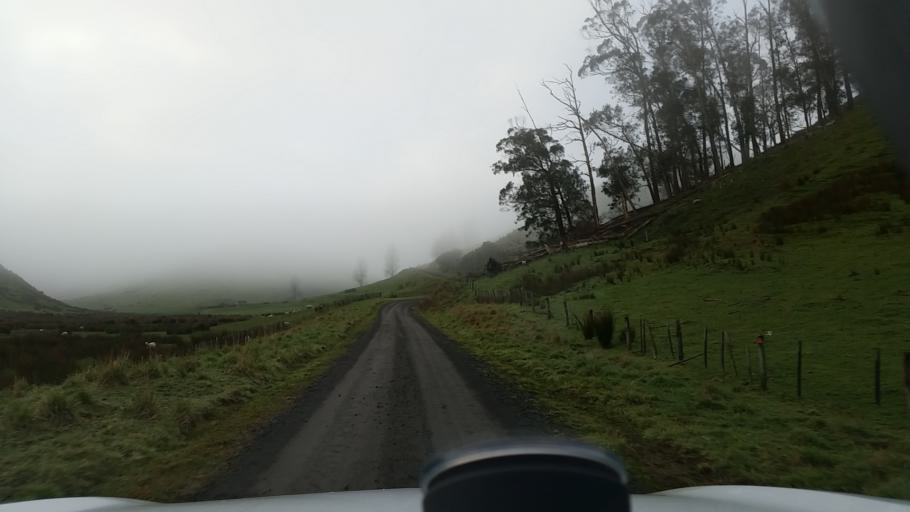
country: NZ
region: Taranaki
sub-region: South Taranaki District
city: Eltham
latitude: -39.4320
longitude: 174.4436
